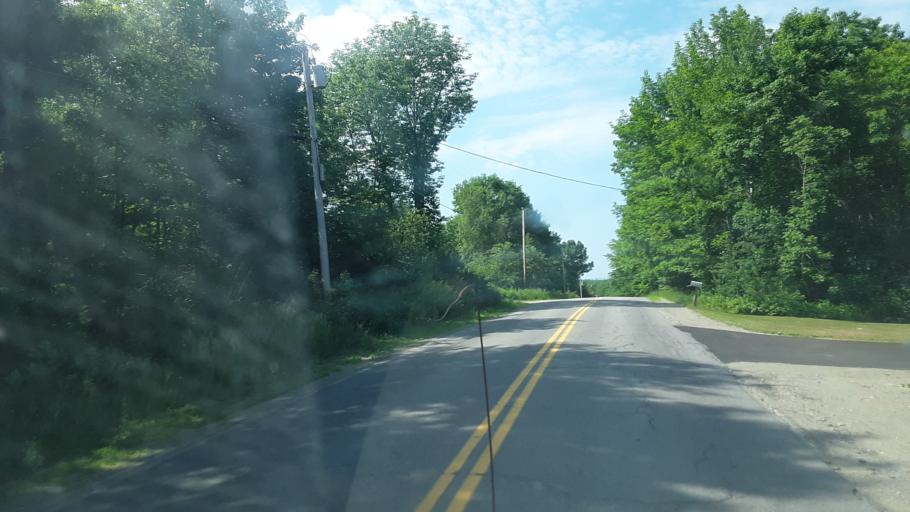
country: US
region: Maine
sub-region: Waldo County
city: Swanville
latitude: 44.5740
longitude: -68.9499
